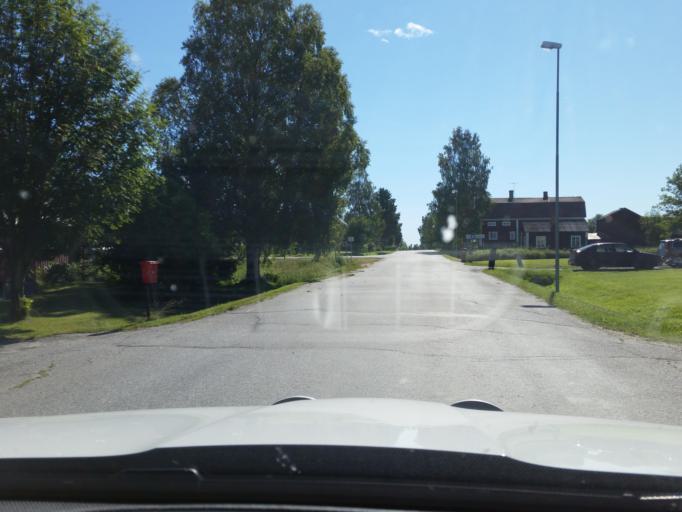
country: SE
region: Norrbotten
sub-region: Pitea Kommun
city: Roknas
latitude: 65.3409
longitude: 21.2215
